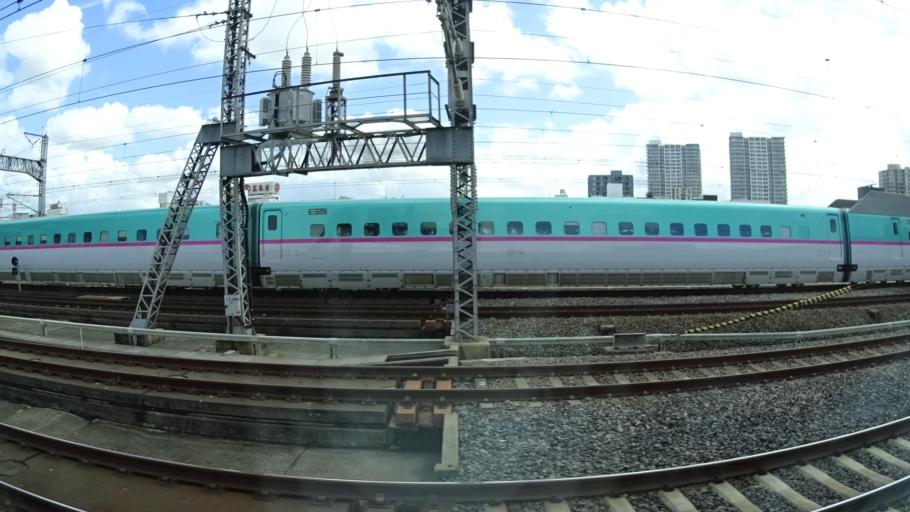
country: JP
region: Saitama
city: Yono
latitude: 35.9056
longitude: 139.6233
